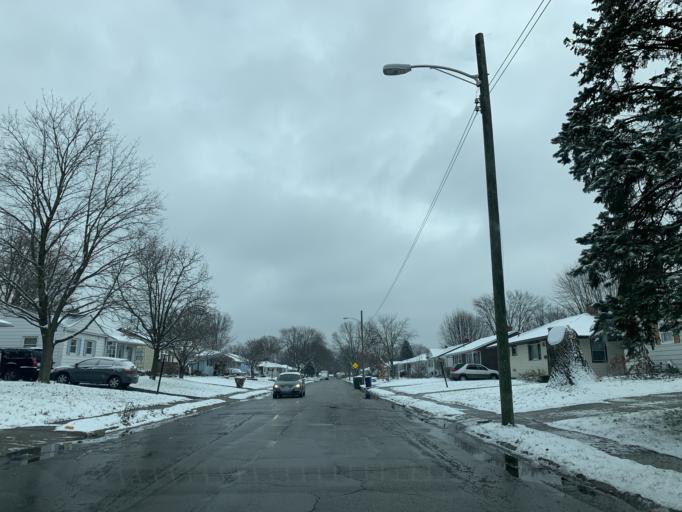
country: US
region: Ohio
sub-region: Franklin County
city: Minerva Park
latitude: 40.0540
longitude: -82.9675
